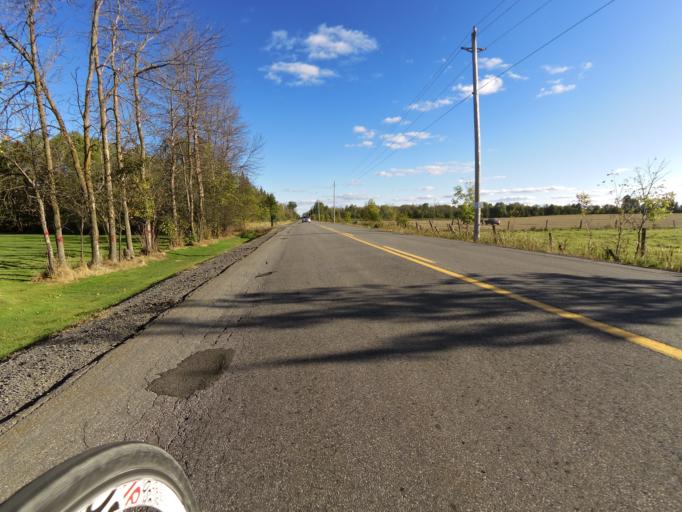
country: CA
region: Ontario
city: Bells Corners
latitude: 45.1761
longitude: -75.8041
